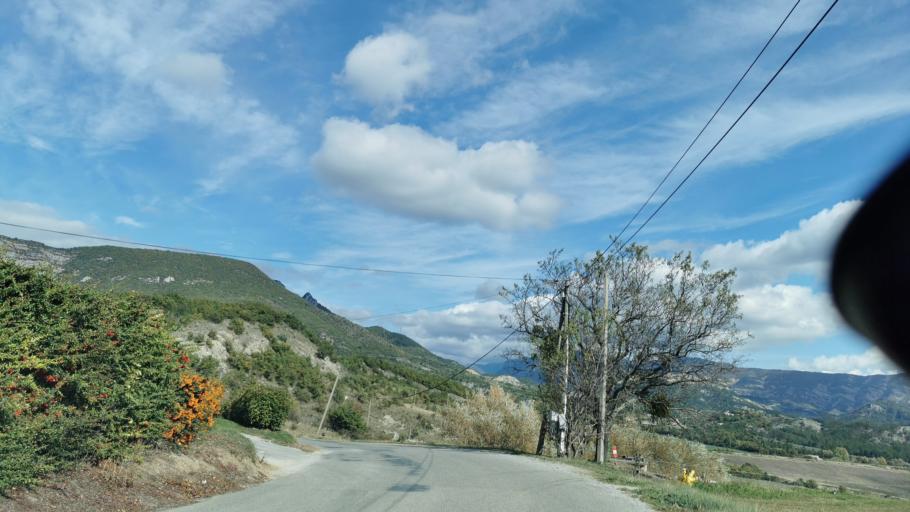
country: FR
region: Provence-Alpes-Cote d'Azur
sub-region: Departement des Alpes-de-Haute-Provence
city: Sisteron
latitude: 44.1806
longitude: 5.9839
